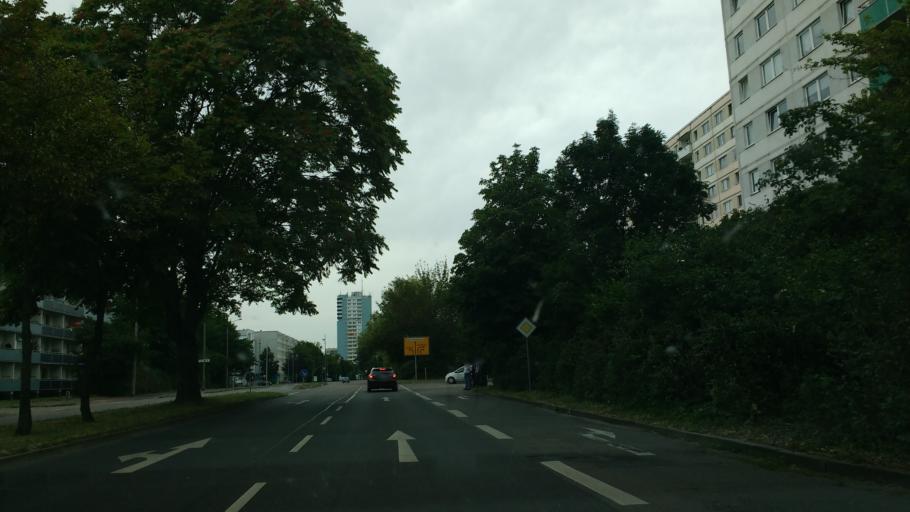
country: DE
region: Saxony-Anhalt
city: Halle Neustadt
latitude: 51.4790
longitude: 11.9356
